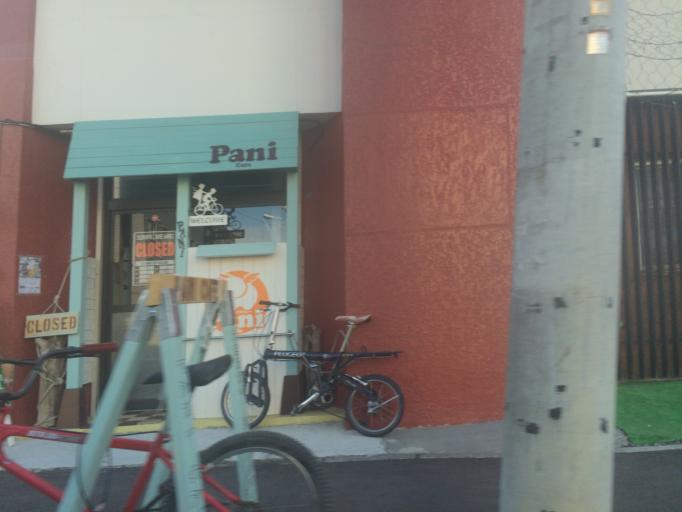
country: JP
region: Hokkaido
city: Sapporo
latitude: 43.0340
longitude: 141.3516
